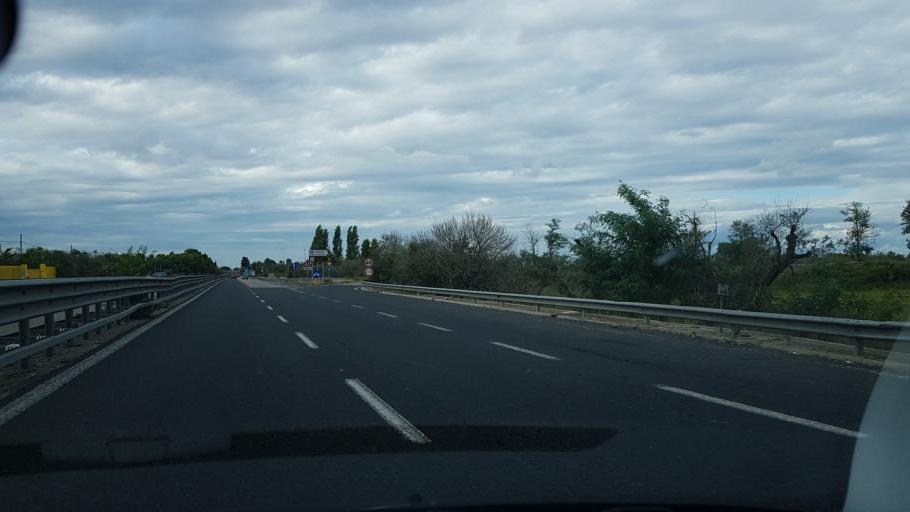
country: IT
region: Apulia
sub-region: Provincia di Lecce
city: Cavallino
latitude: 40.2997
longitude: 18.1938
